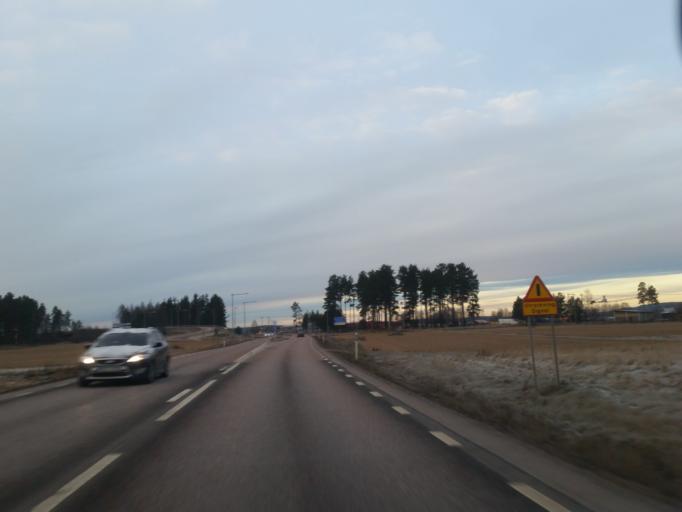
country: SE
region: Dalarna
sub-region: Leksand Municipality
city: Leksand
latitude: 60.7174
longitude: 15.0252
